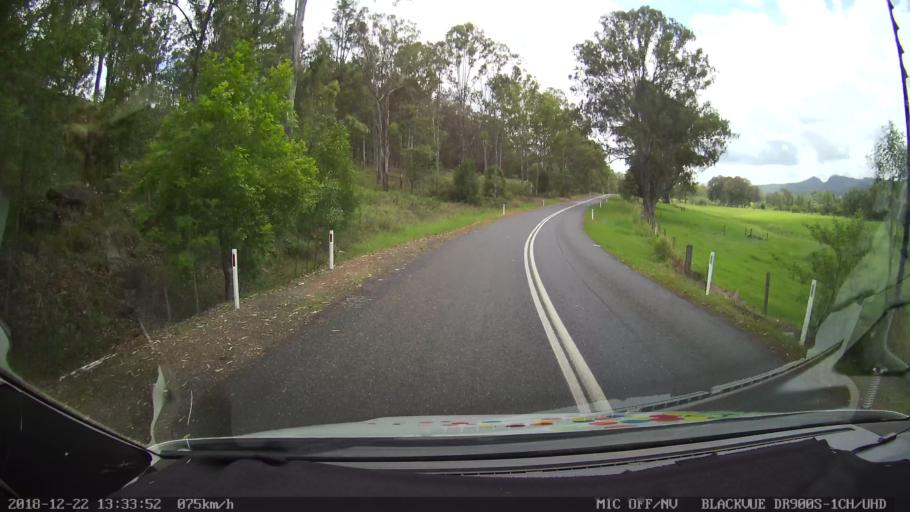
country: AU
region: New South Wales
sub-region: Clarence Valley
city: Coutts Crossing
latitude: -29.8659
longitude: 152.8235
